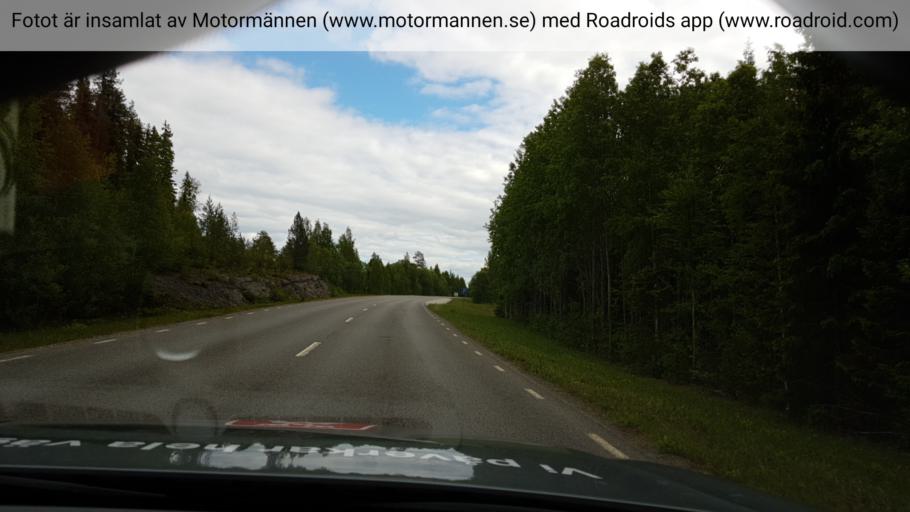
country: SE
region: Jaemtland
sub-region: Stroemsunds Kommun
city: Stroemsund
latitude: 64.3159
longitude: 15.2109
